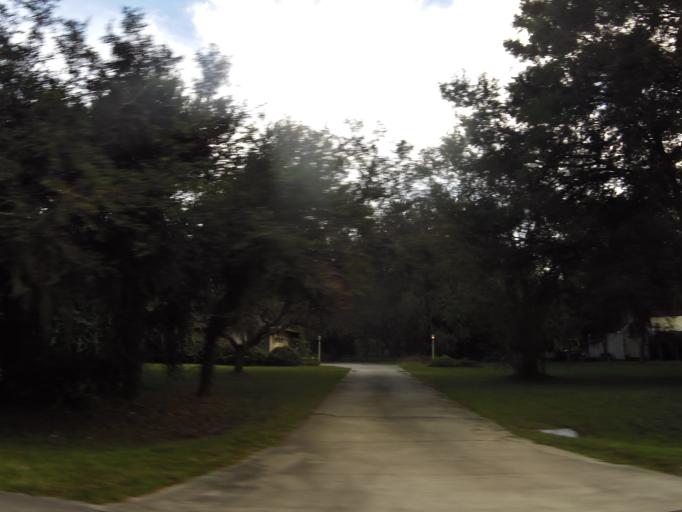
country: US
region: Florida
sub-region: Saint Johns County
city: Fruit Cove
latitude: 30.0957
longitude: -81.6225
